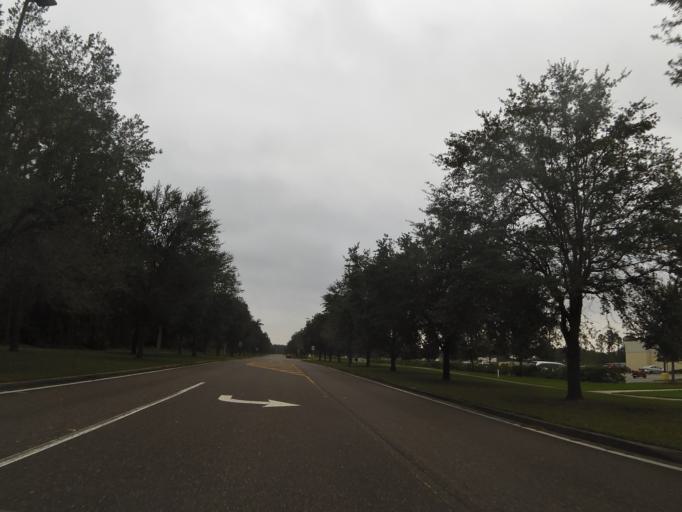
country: US
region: Florida
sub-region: Duval County
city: Baldwin
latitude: 30.2354
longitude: -81.8832
